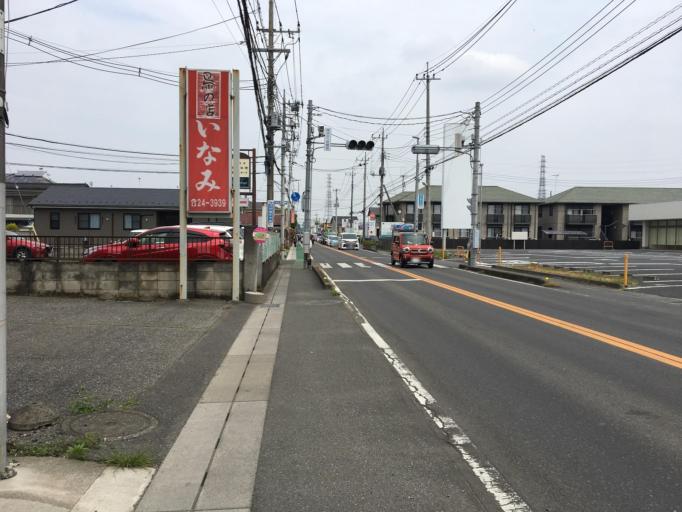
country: JP
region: Tochigi
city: Oyama
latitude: 36.3258
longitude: 139.8093
